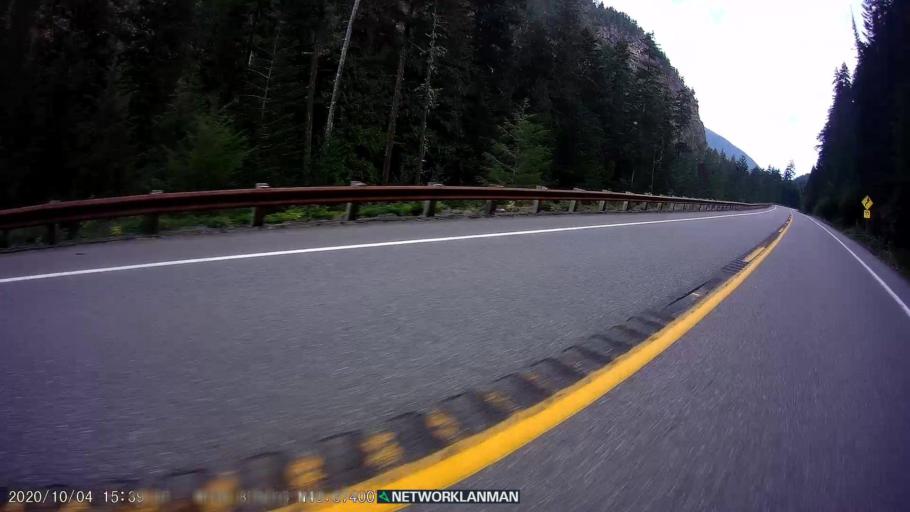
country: US
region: Washington
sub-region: Snohomish County
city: Darrington
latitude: 48.6738
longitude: -120.8793
